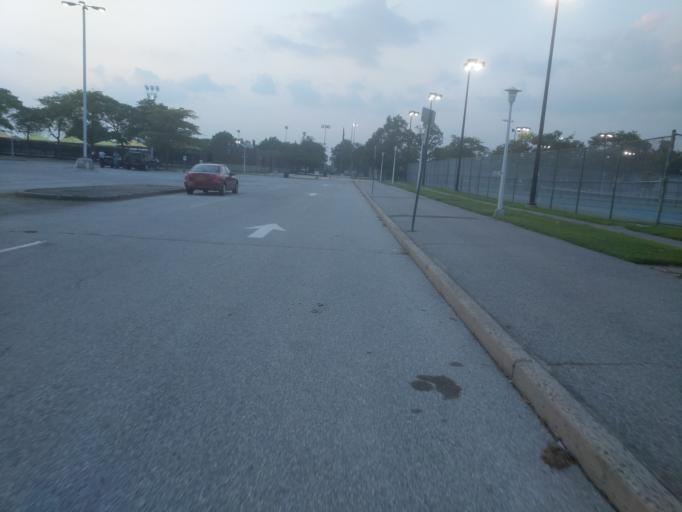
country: US
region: New York
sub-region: Nassau County
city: South Valley Stream
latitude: 40.6449
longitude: -73.7363
